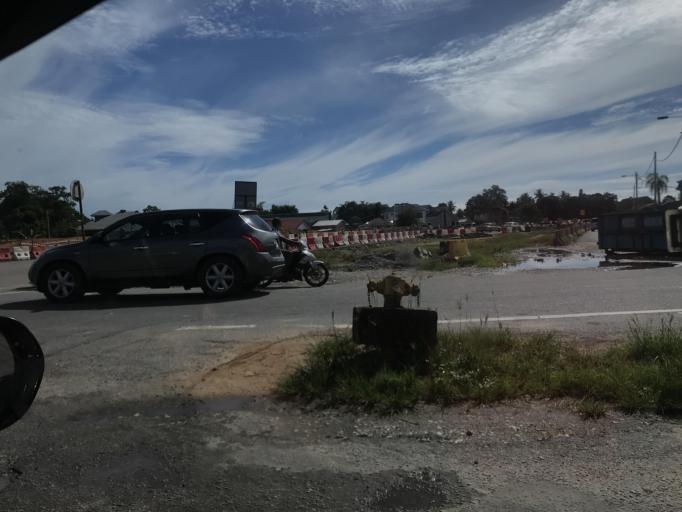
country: MY
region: Kelantan
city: Kota Bharu
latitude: 6.1227
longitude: 102.1999
